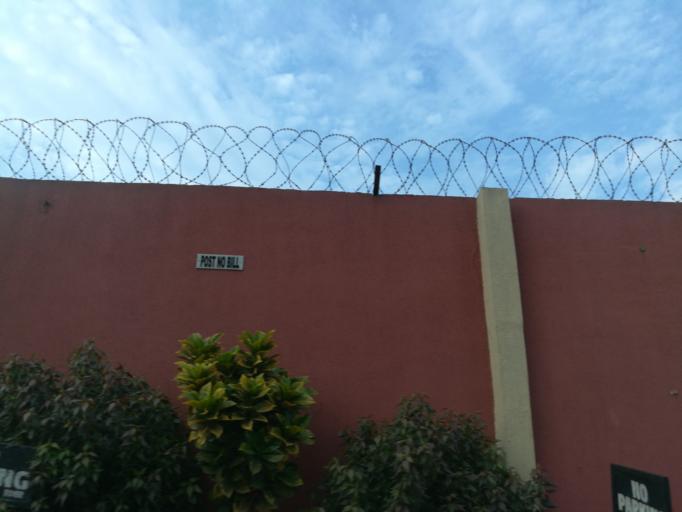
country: NG
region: Lagos
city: Ikeja
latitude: 6.6005
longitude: 3.3443
